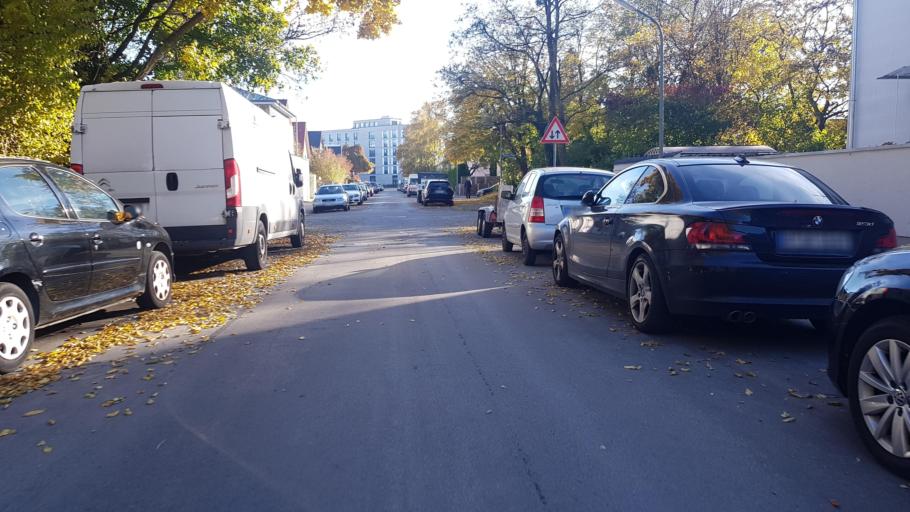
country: DE
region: Bavaria
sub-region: Upper Bavaria
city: Karlsfeld
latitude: 48.1826
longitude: 11.5009
